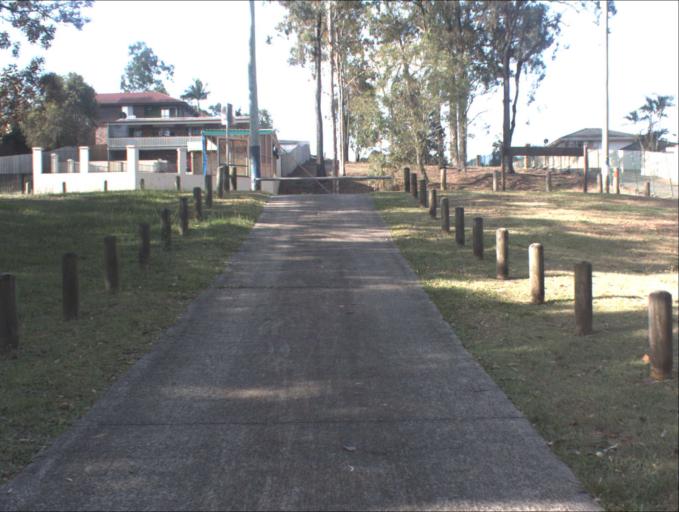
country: AU
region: Queensland
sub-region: Logan
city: Beenleigh
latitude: -27.6798
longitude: 153.2051
